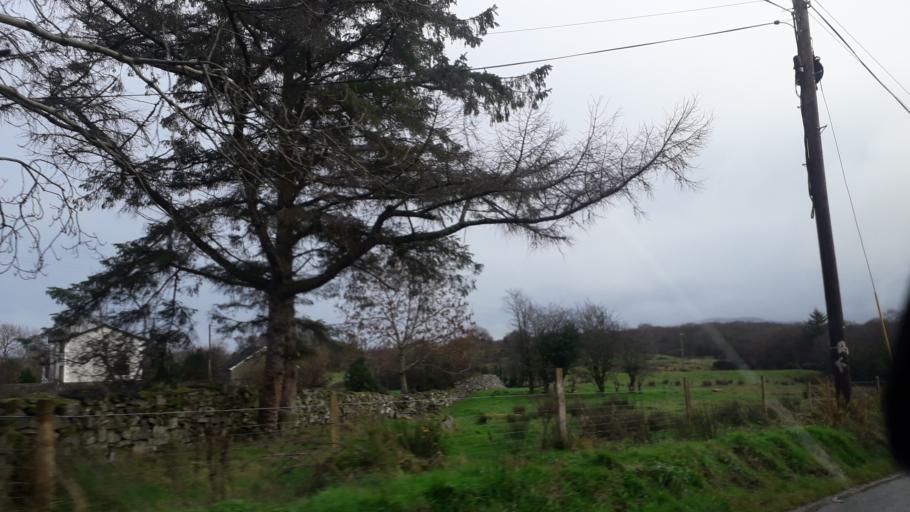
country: IE
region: Ulster
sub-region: County Donegal
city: Buncrana
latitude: 55.1335
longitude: -7.5317
